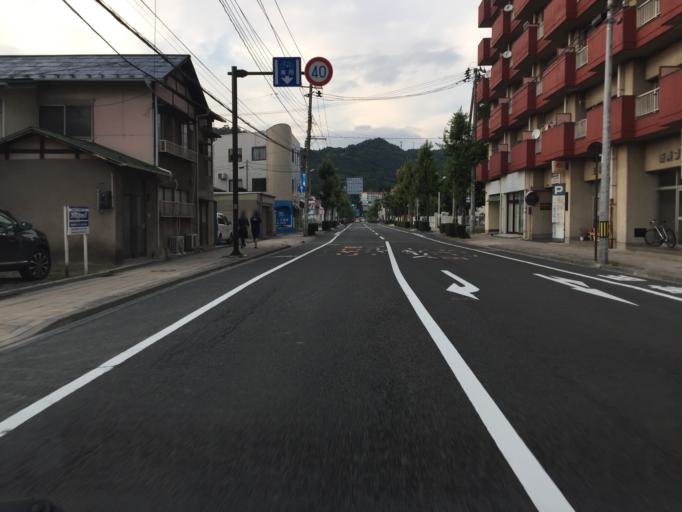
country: JP
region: Fukushima
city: Fukushima-shi
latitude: 37.7600
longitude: 140.4681
